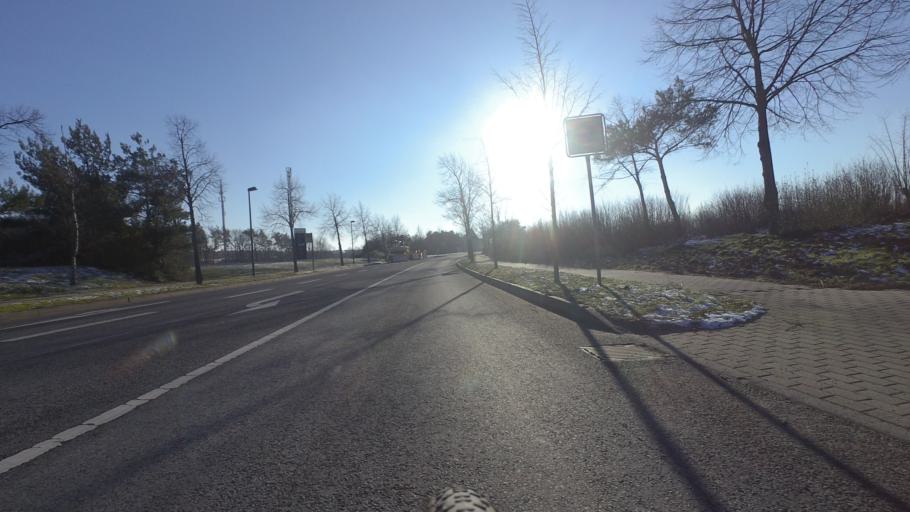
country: DE
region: Brandenburg
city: Ludwigsfelde
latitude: 52.3136
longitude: 13.2920
